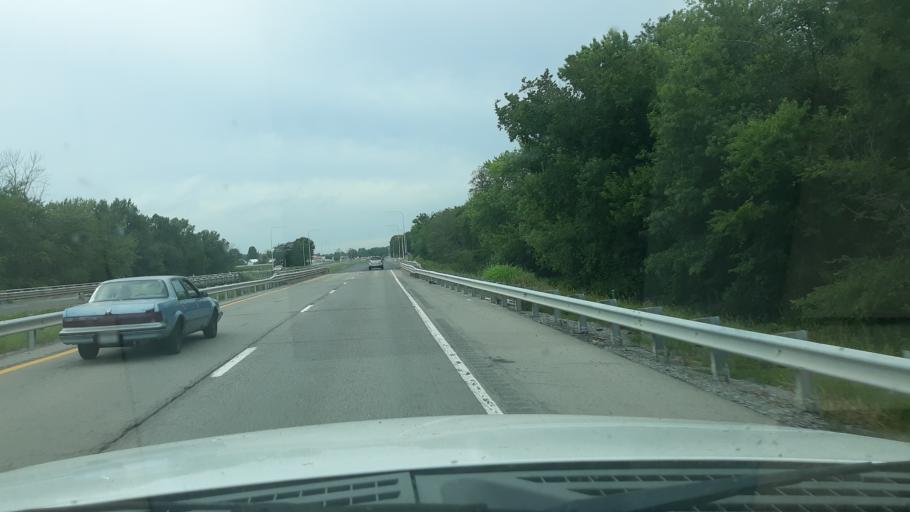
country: US
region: Illinois
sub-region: Williamson County
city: Marion
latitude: 37.7316
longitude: -88.8877
